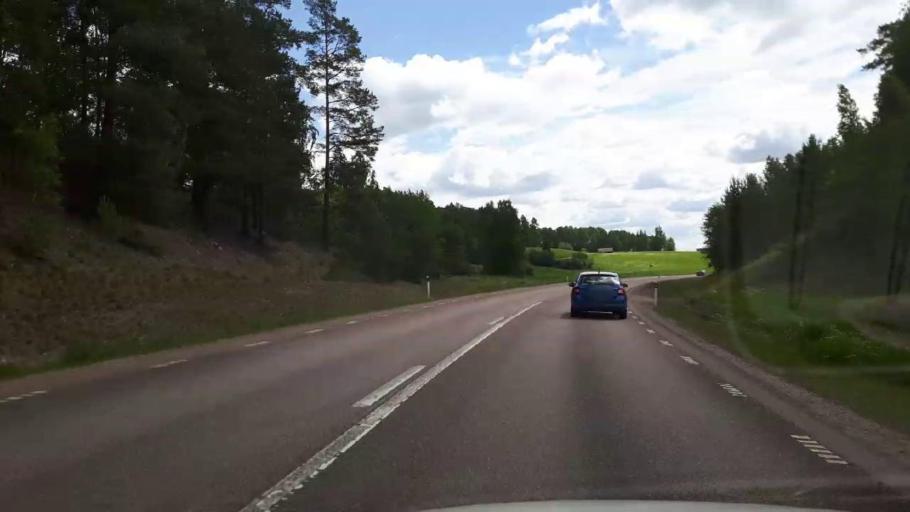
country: SE
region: Dalarna
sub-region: Saters Kommun
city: Saeter
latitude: 60.4339
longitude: 15.8284
